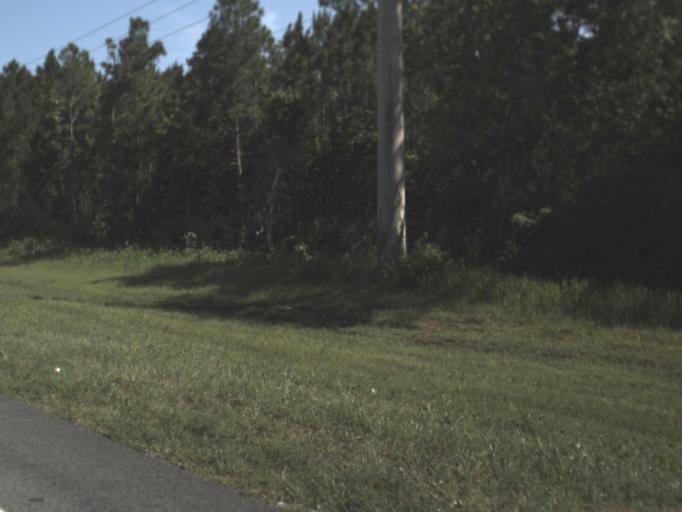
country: US
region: Florida
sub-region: Saint Johns County
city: Saint Augustine
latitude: 29.9245
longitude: -81.4197
